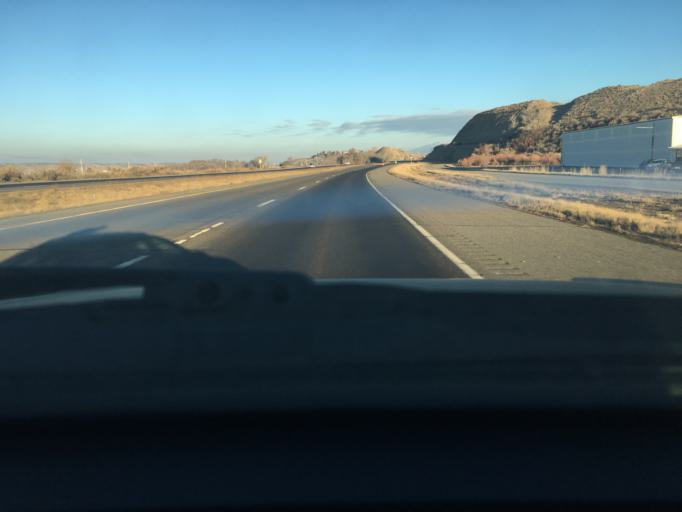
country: US
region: Colorado
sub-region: Montrose County
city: Montrose
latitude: 38.5301
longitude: -107.9350
